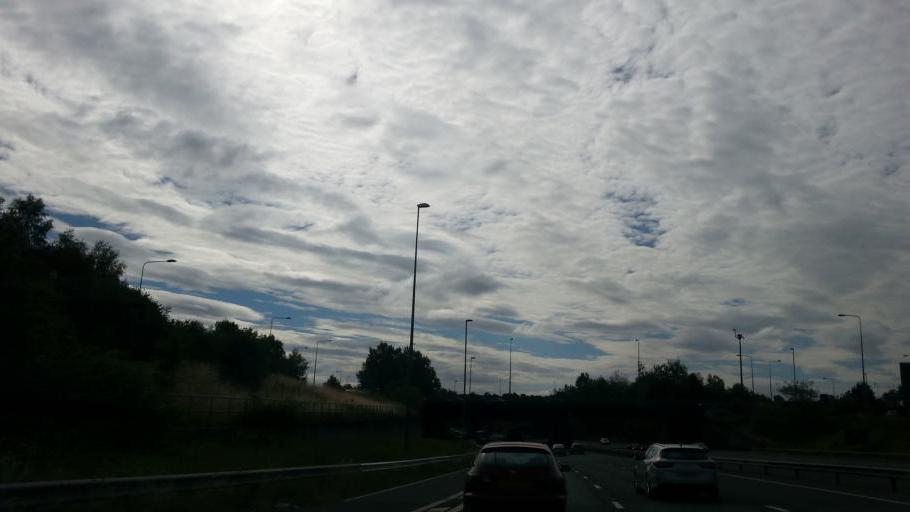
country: GB
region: England
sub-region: Manchester
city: Crumpsall
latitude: 53.5410
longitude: -2.2400
